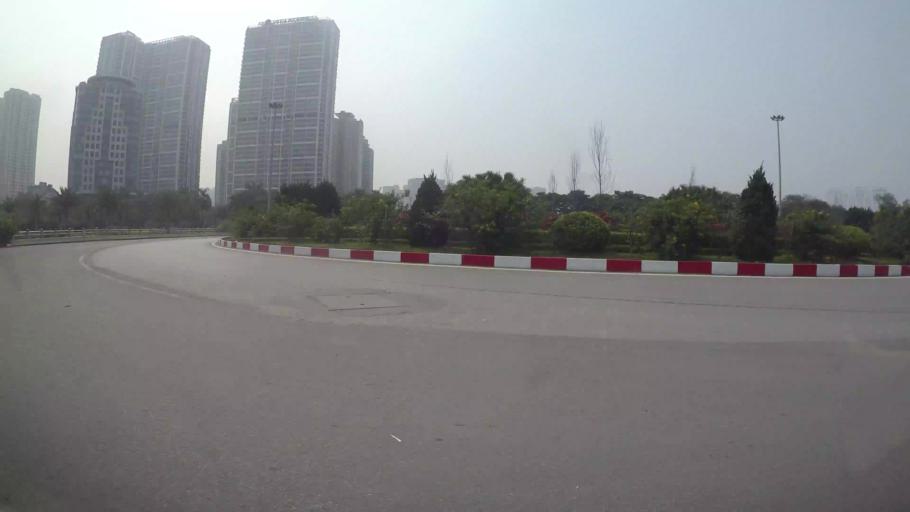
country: VN
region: Ha Noi
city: Thanh Xuan
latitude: 21.0039
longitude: 105.7893
